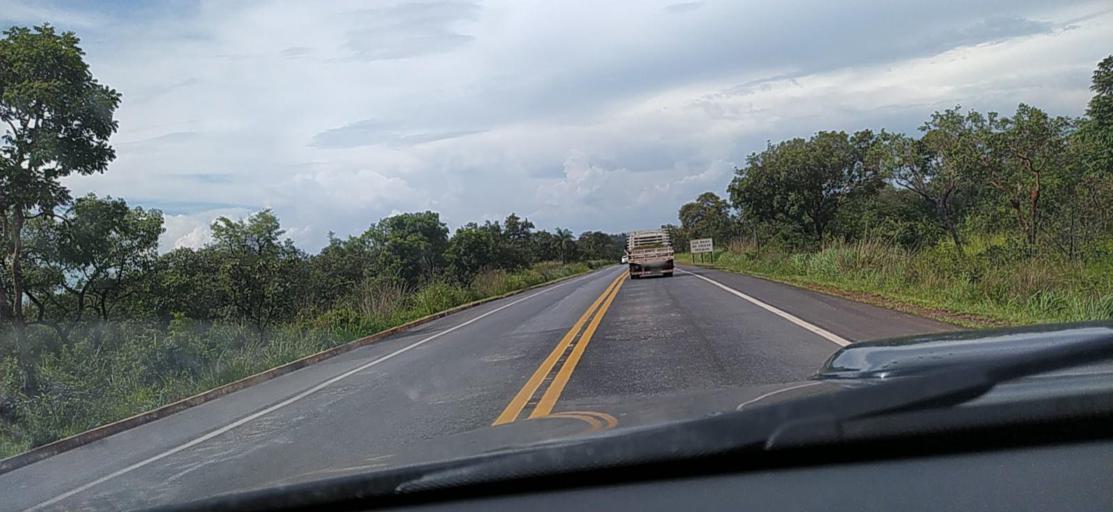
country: BR
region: Minas Gerais
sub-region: Montes Claros
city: Montes Claros
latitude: -16.8620
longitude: -43.8535
